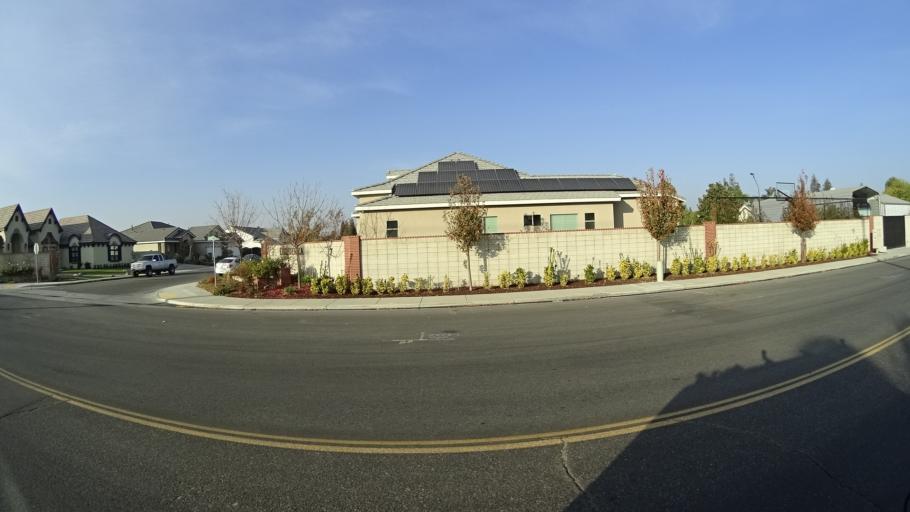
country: US
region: California
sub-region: Kern County
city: Rosedale
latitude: 35.3724
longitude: -119.1279
